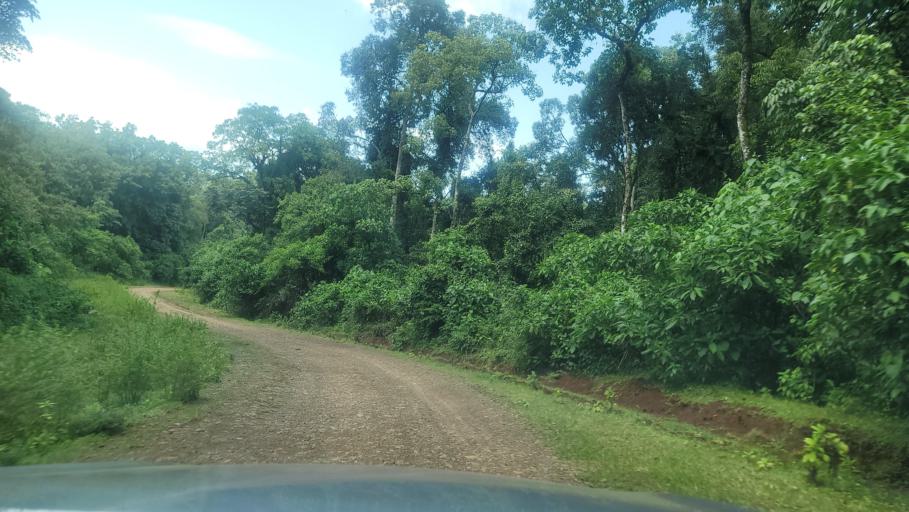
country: ET
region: Southern Nations, Nationalities, and People's Region
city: Bonga
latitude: 7.6734
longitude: 36.2424
